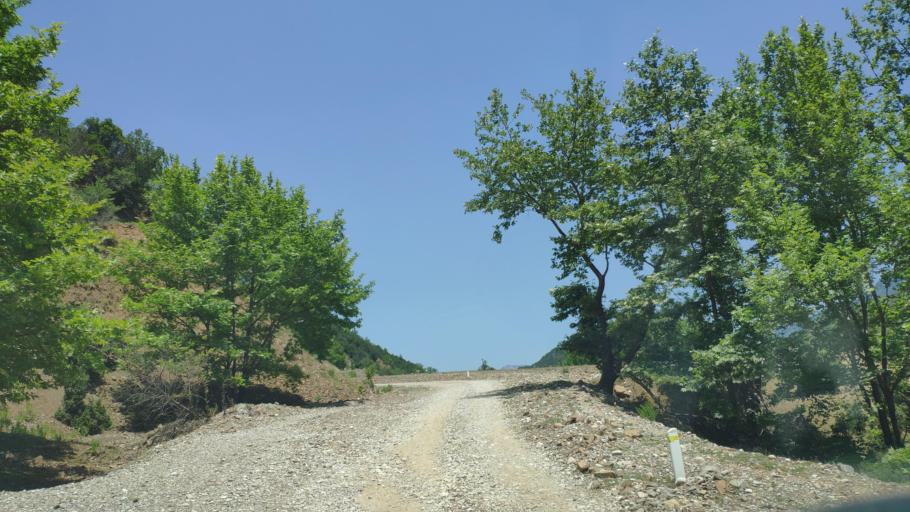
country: GR
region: Thessaly
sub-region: Nomos Kardhitsas
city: Anthiro
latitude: 39.1699
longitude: 21.3715
